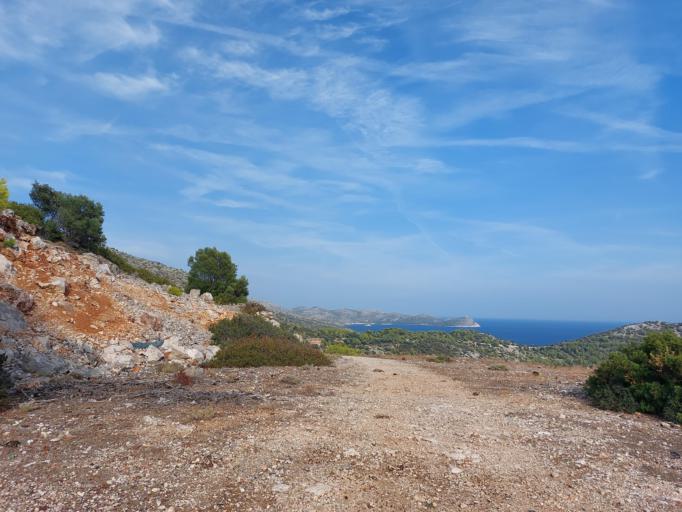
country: HR
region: Dubrovacko-Neretvanska
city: Smokvica
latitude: 42.7329
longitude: 16.8309
